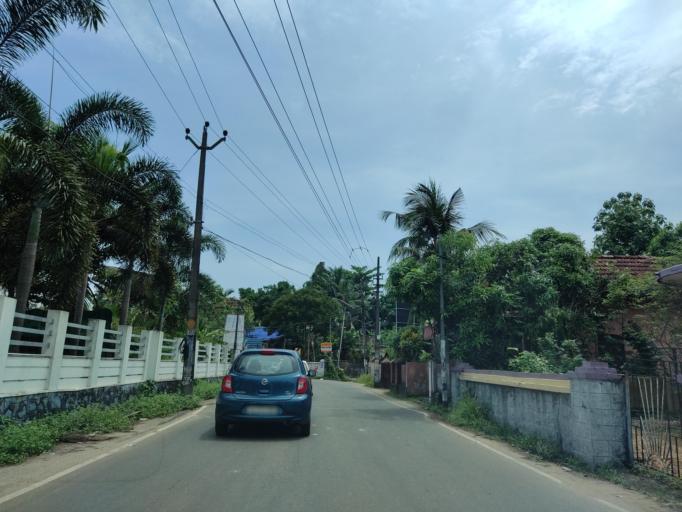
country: IN
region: Kerala
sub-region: Alappuzha
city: Chengannur
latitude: 9.3162
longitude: 76.6069
